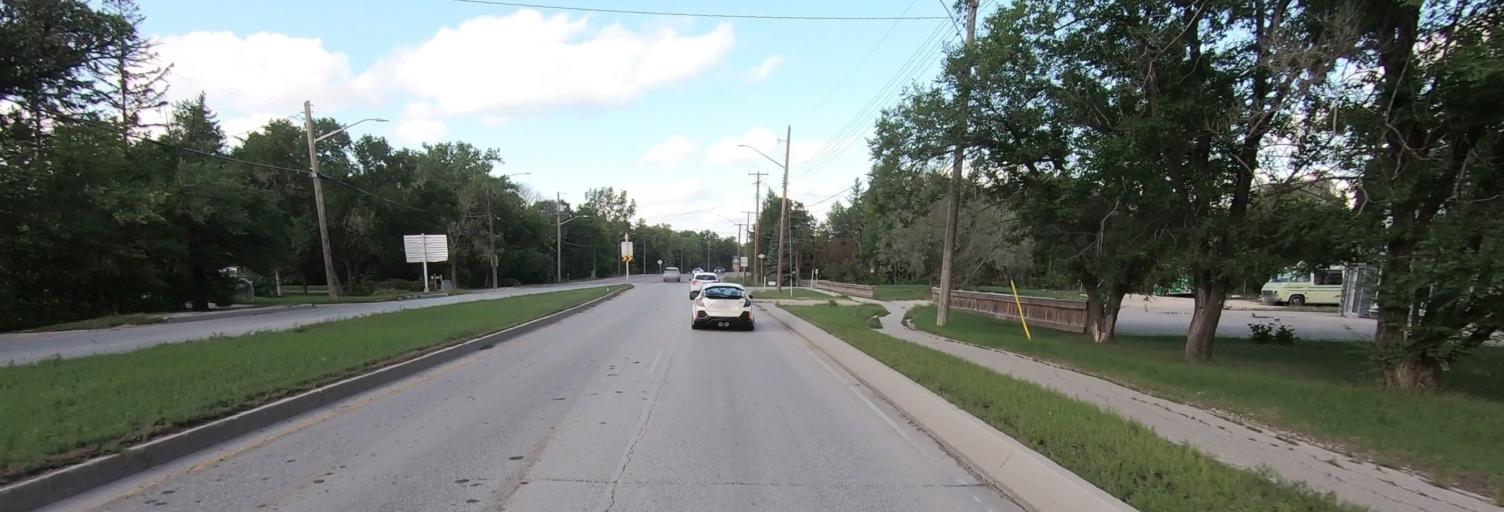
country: CA
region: Manitoba
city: Winnipeg
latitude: 49.9698
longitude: -97.0624
